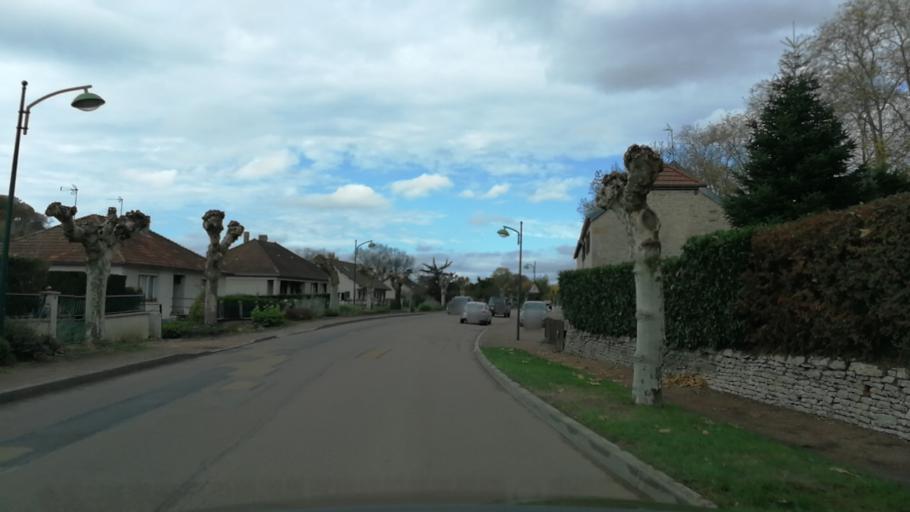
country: FR
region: Bourgogne
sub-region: Departement de la Cote-d'Or
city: Pouilly-en-Auxois
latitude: 47.2571
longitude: 4.5610
